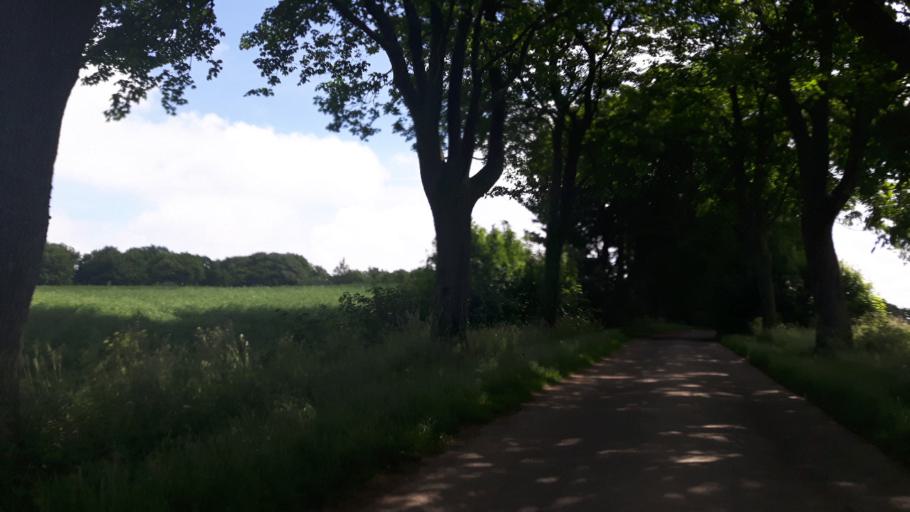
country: PL
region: West Pomeranian Voivodeship
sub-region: Powiat slawienski
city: Darlowo
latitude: 54.4652
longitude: 16.5002
